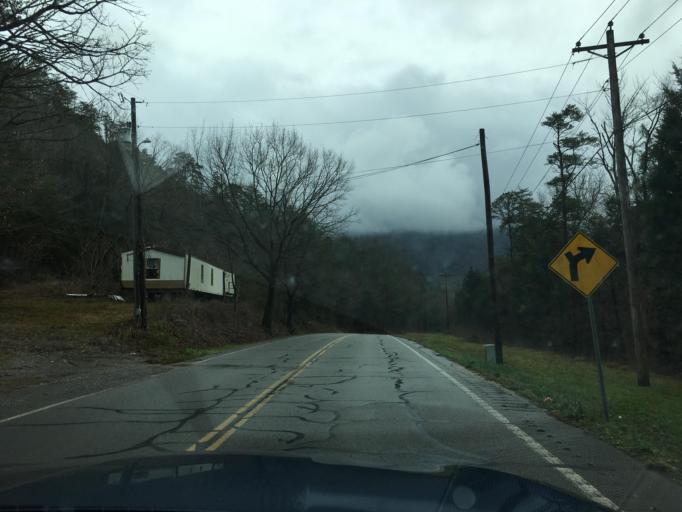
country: US
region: Tennessee
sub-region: Polk County
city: Benton
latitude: 35.1661
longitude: -84.6364
